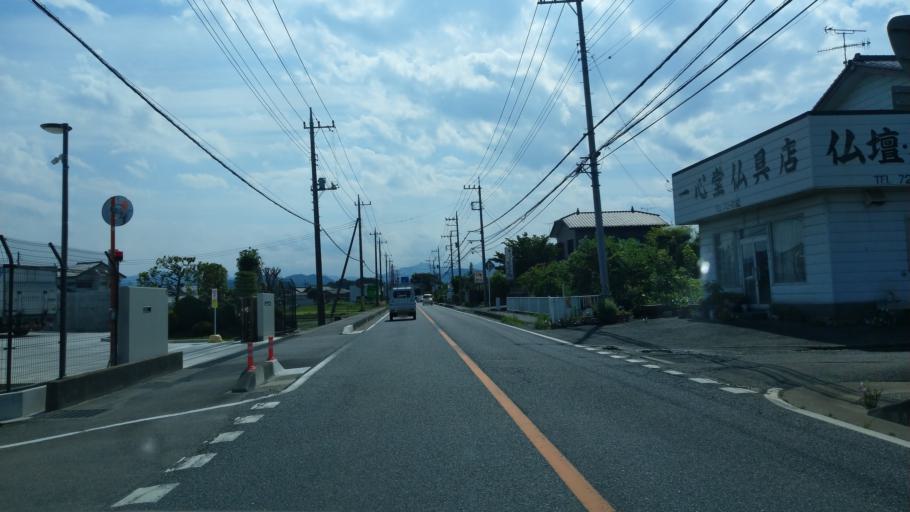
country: JP
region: Saitama
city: Kodamacho-kodamaminami
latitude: 36.2124
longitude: 139.1552
